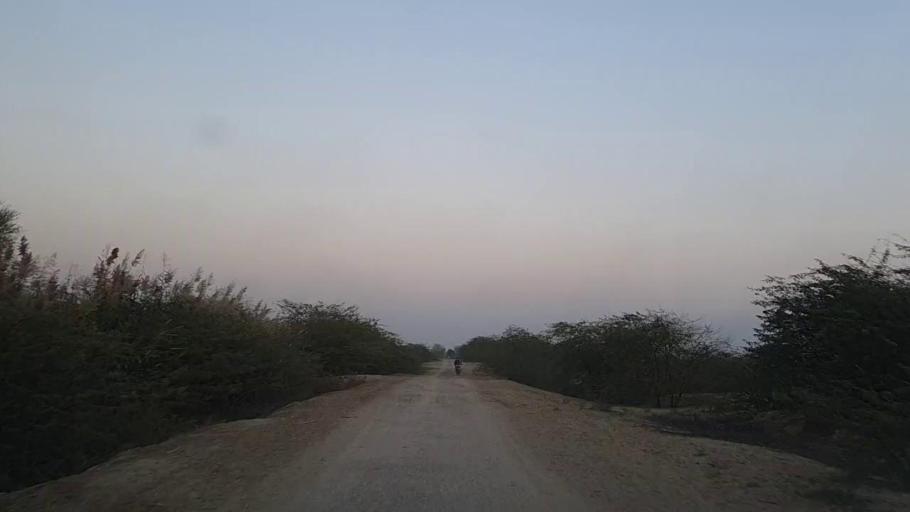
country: PK
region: Sindh
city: Bandhi
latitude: 26.6047
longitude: 68.3703
